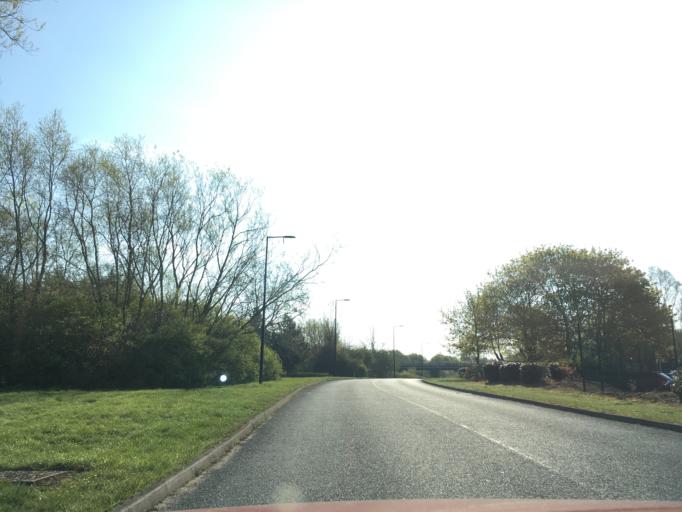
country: GB
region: England
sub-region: Milton Keynes
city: Newport Pagnell
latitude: 52.0702
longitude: -0.7358
